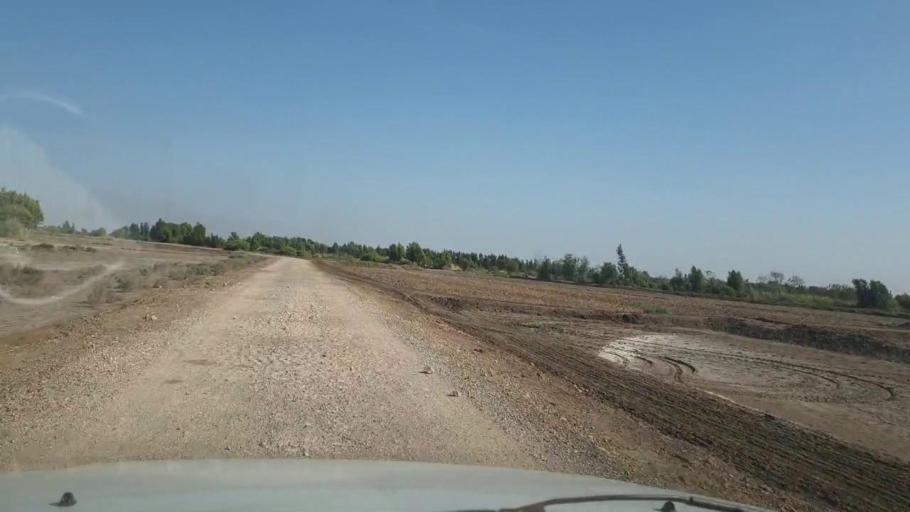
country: PK
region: Sindh
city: Mirpur Sakro
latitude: 24.4845
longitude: 67.8155
